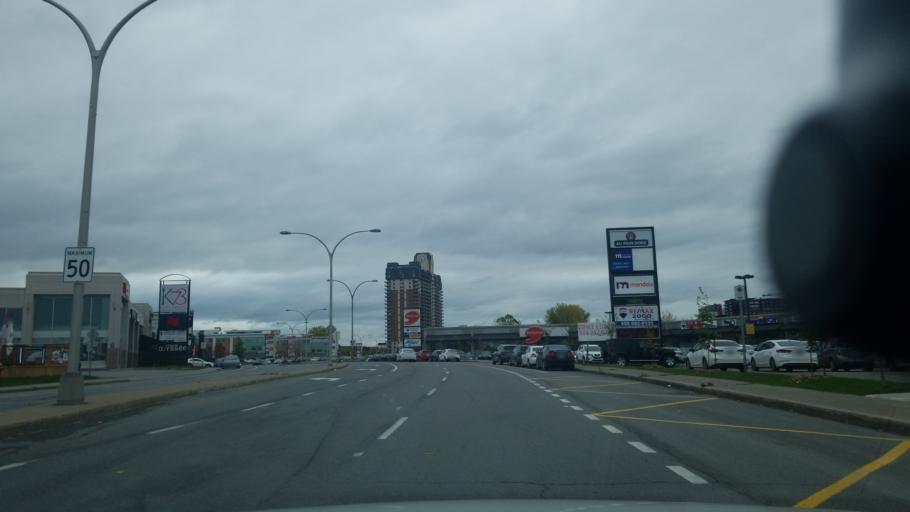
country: CA
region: Quebec
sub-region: Laval
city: Laval
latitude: 45.5667
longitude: -73.7283
